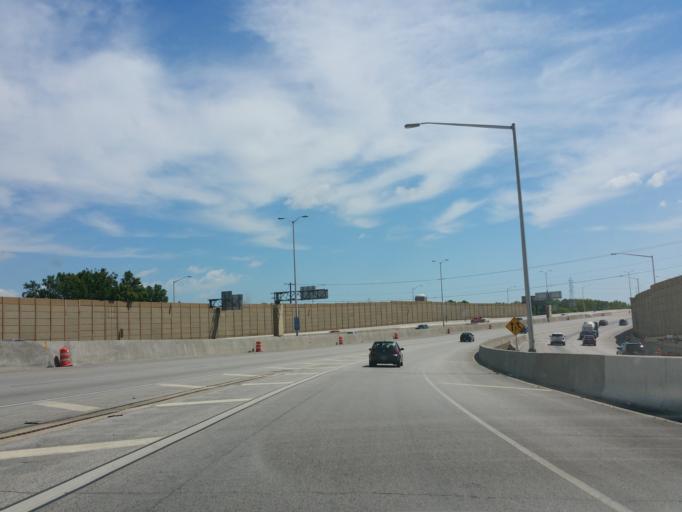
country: US
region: Wisconsin
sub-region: Milwaukee County
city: Saint Francis
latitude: 42.9647
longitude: -87.9324
